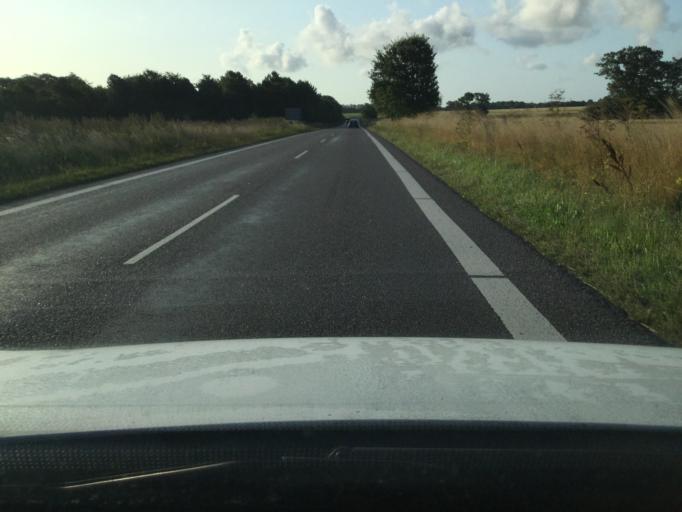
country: DK
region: Zealand
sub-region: Lolland Kommune
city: Rodby
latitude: 54.7893
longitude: 11.2842
